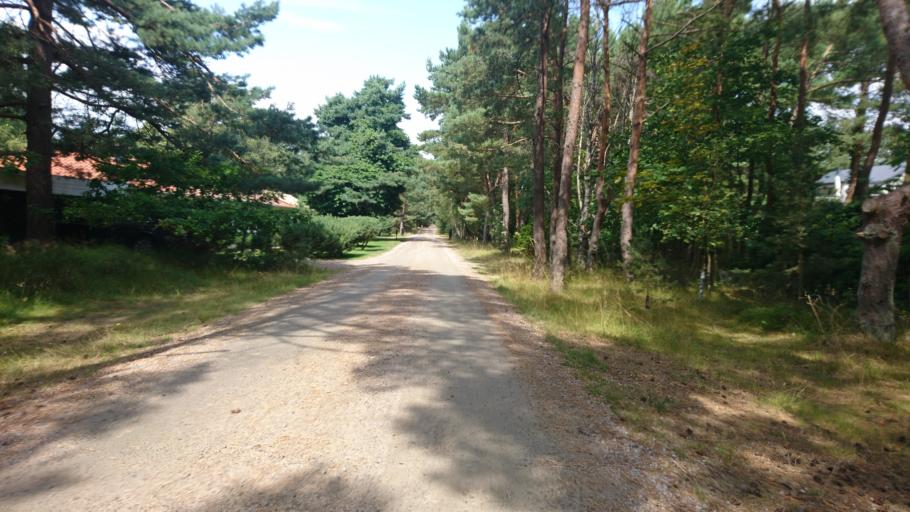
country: SE
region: Skane
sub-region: Vellinge Kommun
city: Ljunghusen
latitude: 55.3895
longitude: 12.9152
